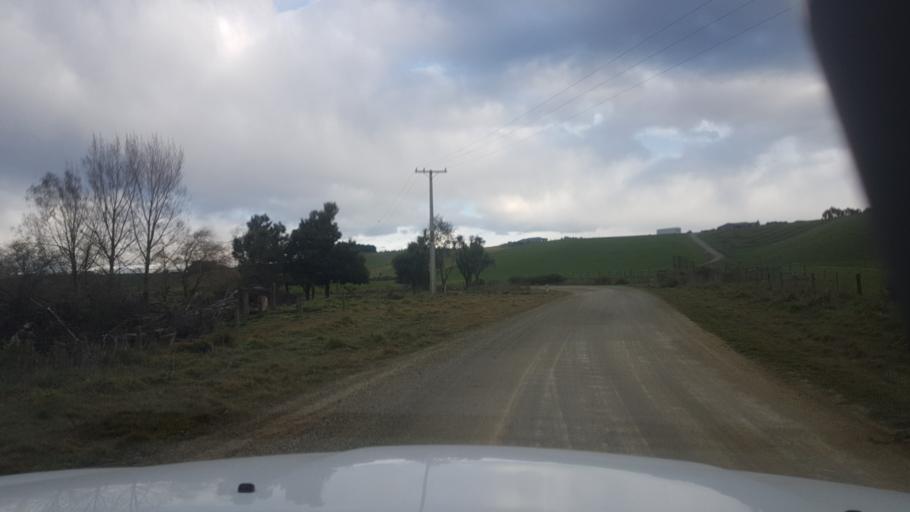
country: NZ
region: Canterbury
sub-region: Timaru District
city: Pleasant Point
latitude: -44.3382
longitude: 171.1801
